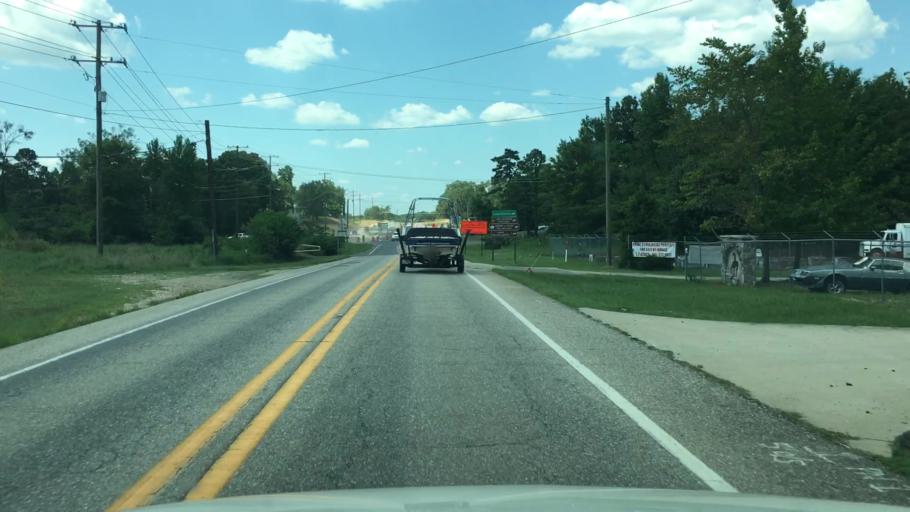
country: US
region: Arkansas
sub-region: Garland County
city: Lake Hamilton
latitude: 34.4114
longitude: -93.0939
